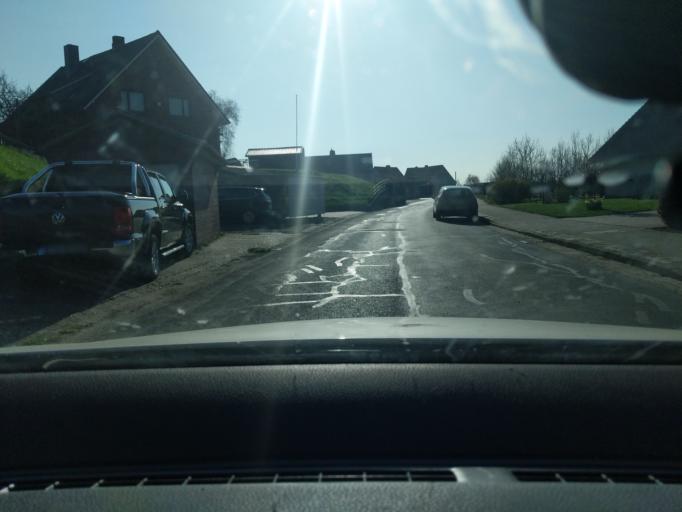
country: DE
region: Lower Saxony
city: Grunendeich
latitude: 53.5654
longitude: 9.6331
